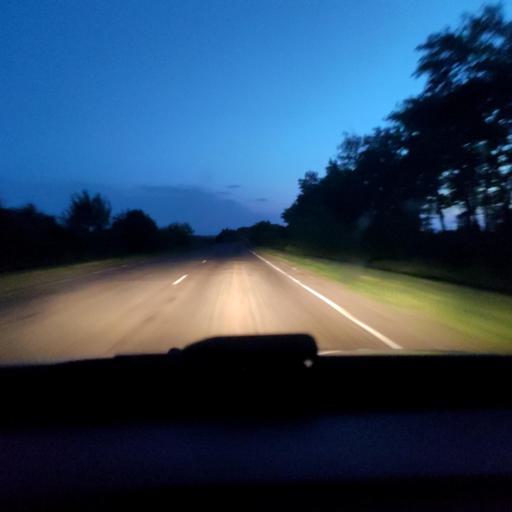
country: RU
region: Voronezj
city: Panino
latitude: 51.6343
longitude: 40.0851
